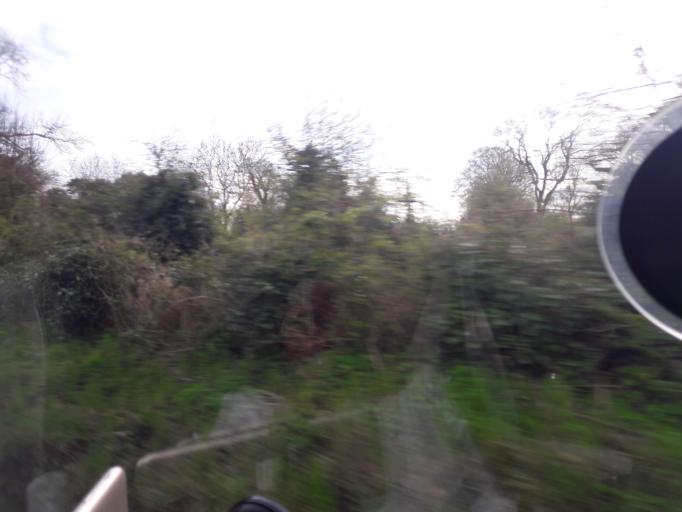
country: IE
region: Leinster
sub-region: An Iarmhi
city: An Muileann gCearr
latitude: 53.5112
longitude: -7.3187
